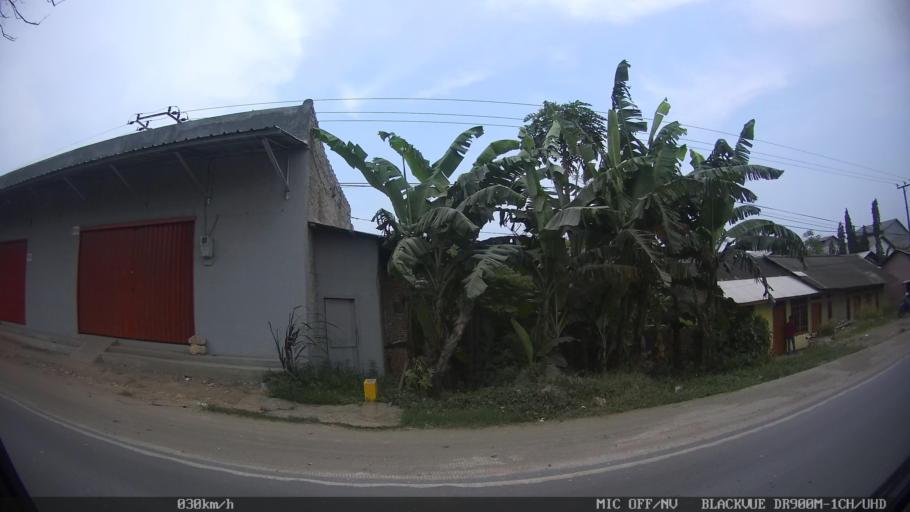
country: ID
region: Lampung
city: Panjang
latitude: -5.4296
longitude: 105.3264
